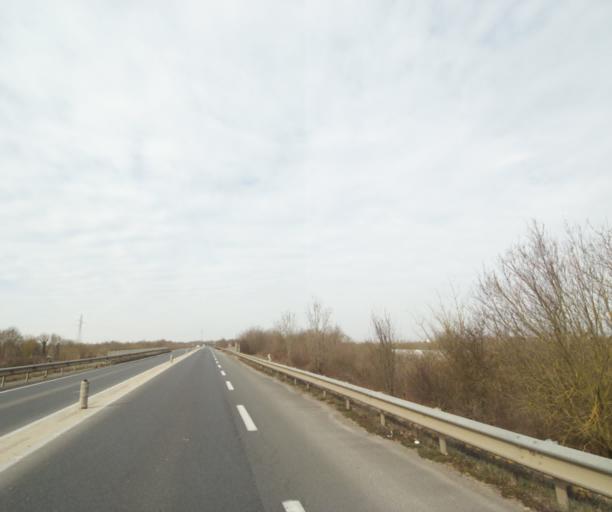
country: FR
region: Poitou-Charentes
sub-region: Departement des Deux-Sevres
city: Niort
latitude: 46.2941
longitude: -0.4576
